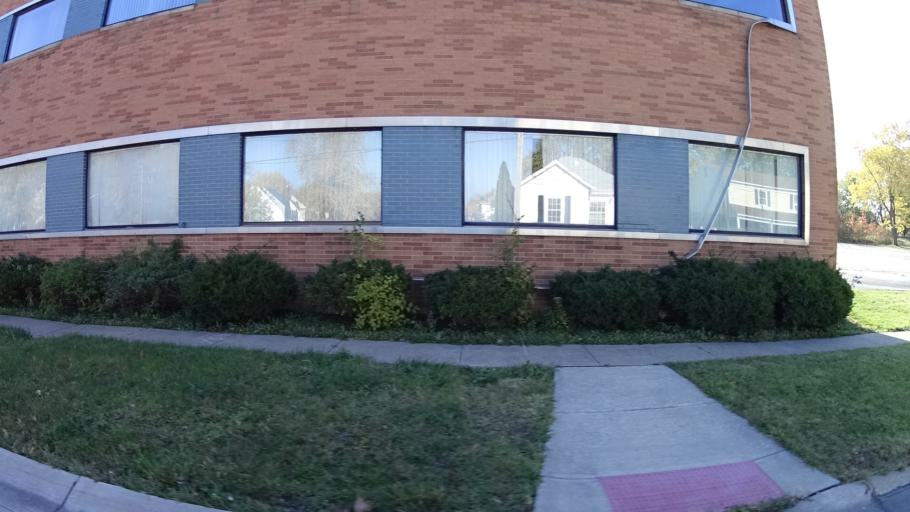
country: US
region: Ohio
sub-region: Lorain County
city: Lorain
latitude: 41.4696
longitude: -82.1609
